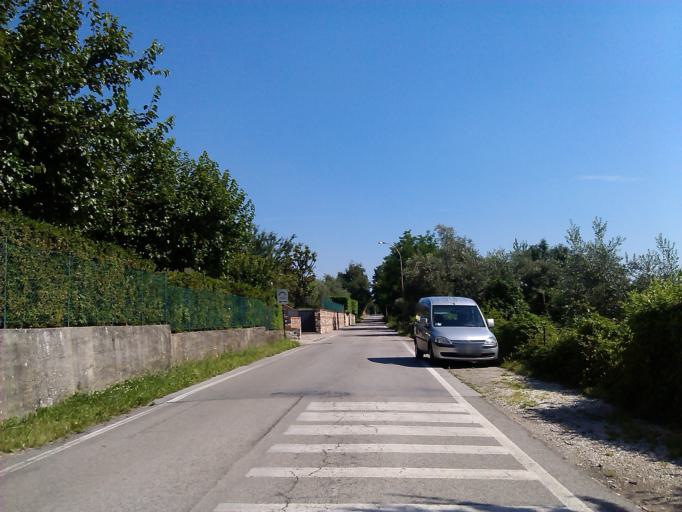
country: IT
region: Veneto
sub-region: Provincia di Vicenza
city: Pove del Grappa
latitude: 45.7978
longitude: 11.7251
